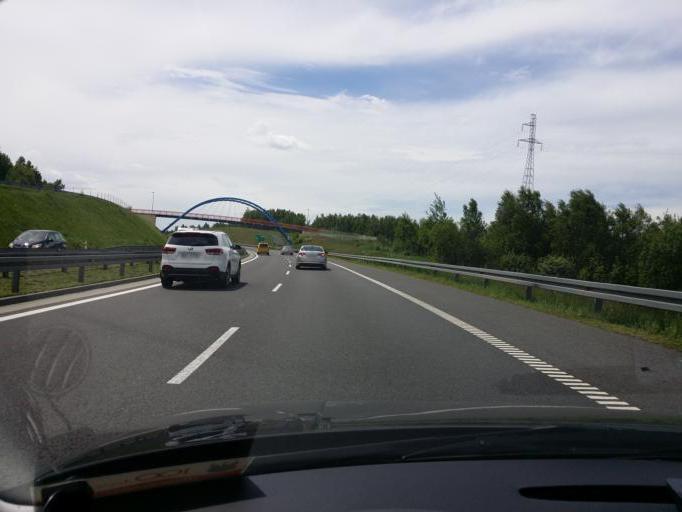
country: PL
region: Swietokrzyskie
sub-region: Powiat kielecki
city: Zagnansk
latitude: 50.9488
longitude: 20.6883
